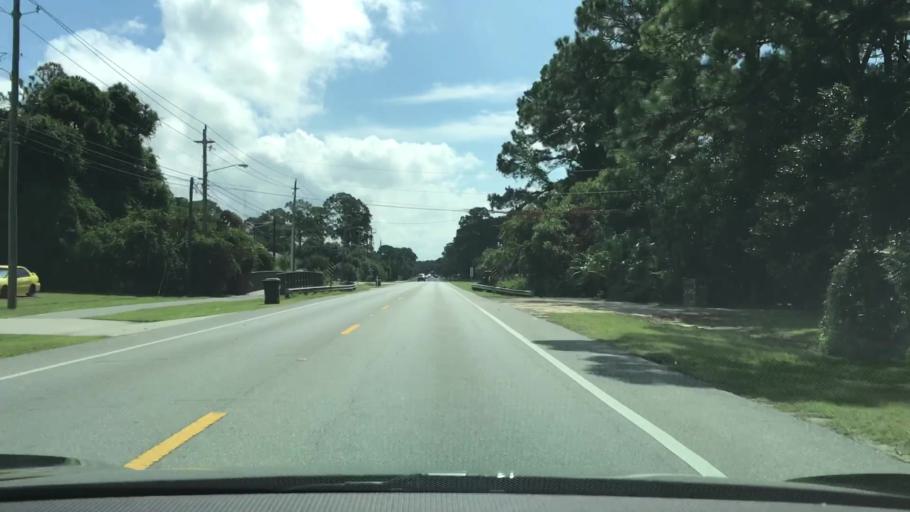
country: US
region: Florida
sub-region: Bay County
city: Panama City Beach
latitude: 30.1669
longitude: -85.7788
